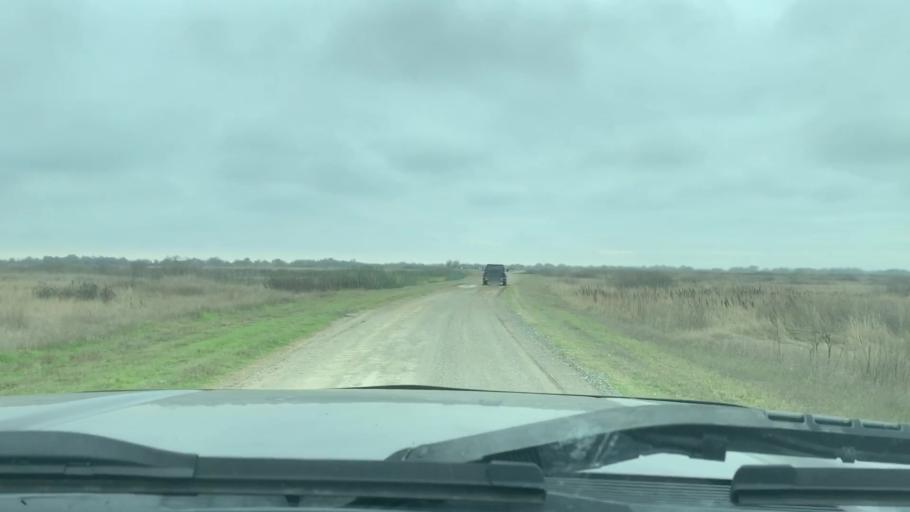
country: US
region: California
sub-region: Merced County
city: Los Banos
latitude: 37.1960
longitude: -120.7937
